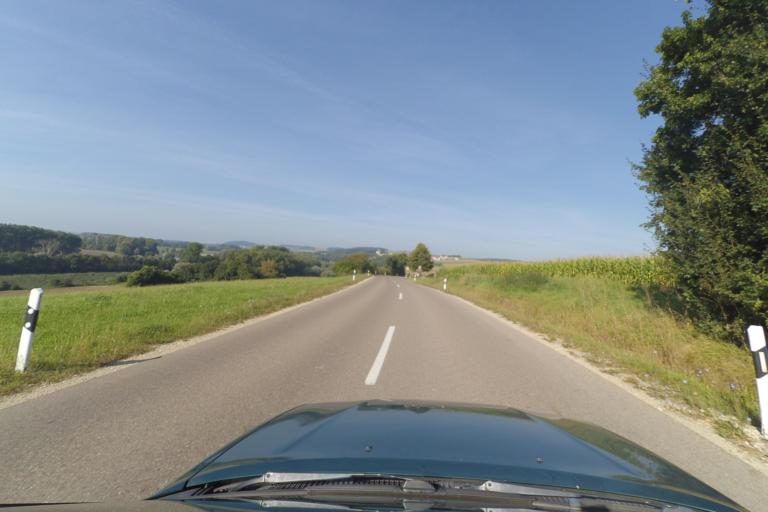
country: DE
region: Bavaria
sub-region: Swabia
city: Niederschonenfeld
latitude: 48.7431
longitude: 10.9065
